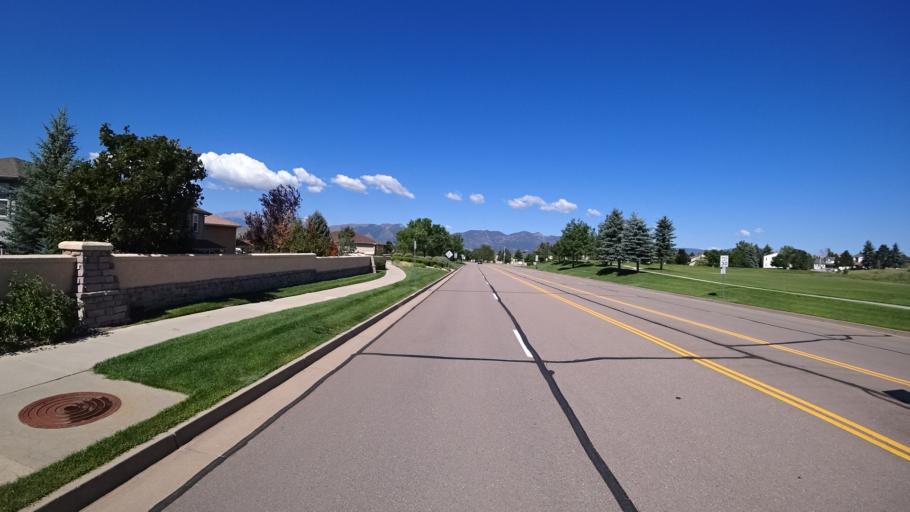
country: US
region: Colorado
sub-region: El Paso County
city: Black Forest
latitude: 38.9757
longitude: -104.7761
